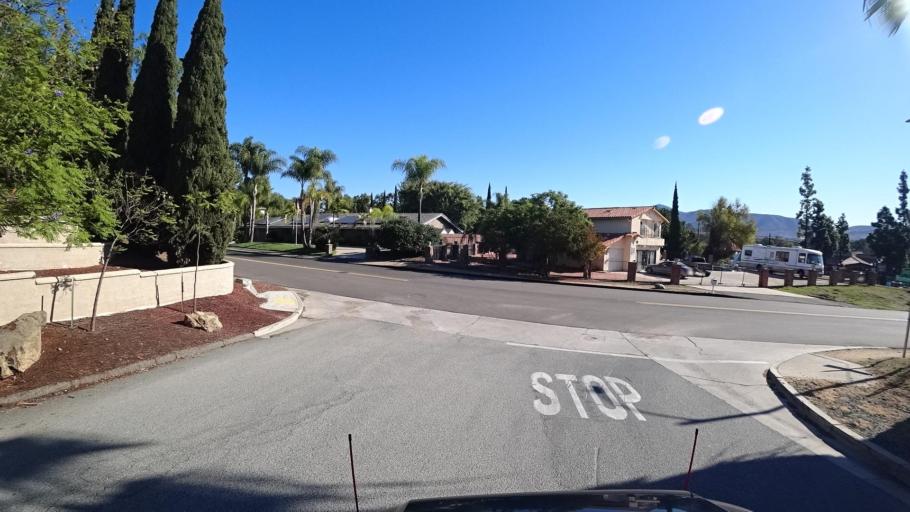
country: US
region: California
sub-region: San Diego County
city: Bonita
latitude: 32.6802
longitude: -117.0166
